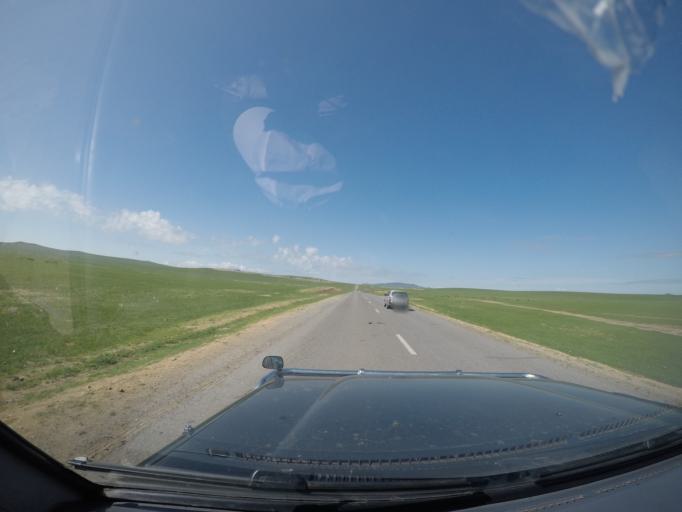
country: MN
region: Suhbaatar
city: Bayasgalant
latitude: 47.3440
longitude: 111.5645
